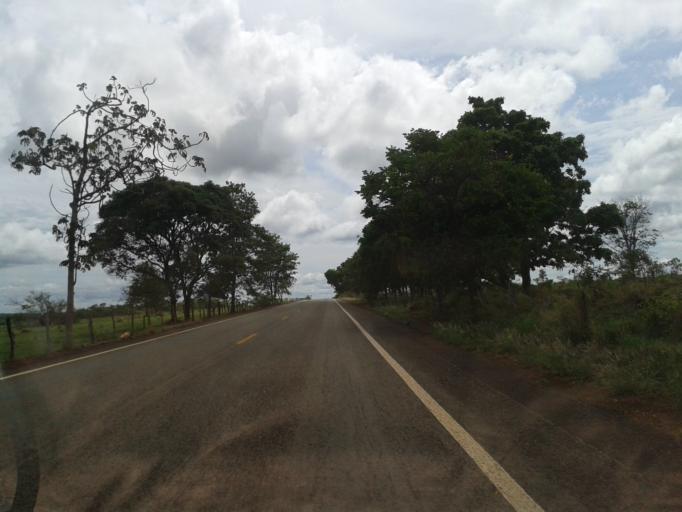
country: BR
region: Goias
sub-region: Buriti Alegre
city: Buriti Alegre
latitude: -18.1274
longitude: -49.1398
